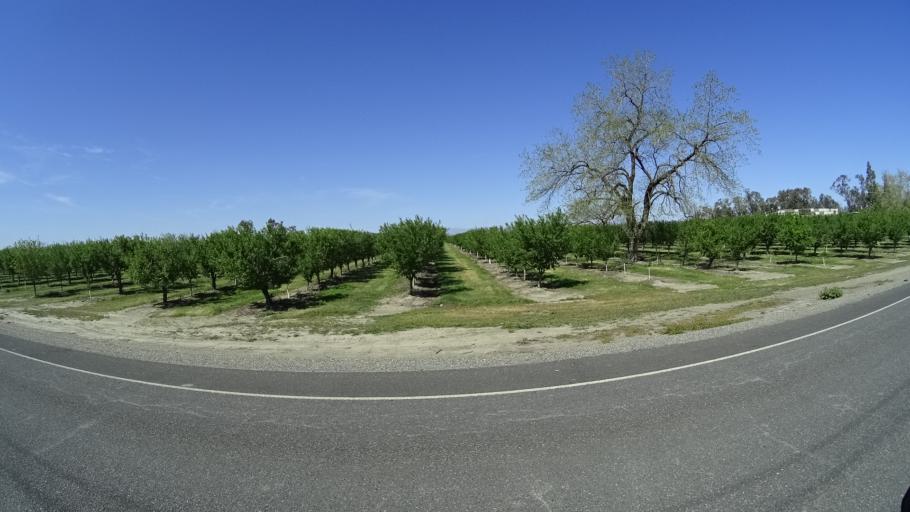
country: US
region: California
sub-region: Glenn County
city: Hamilton City
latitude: 39.7186
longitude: -122.1046
